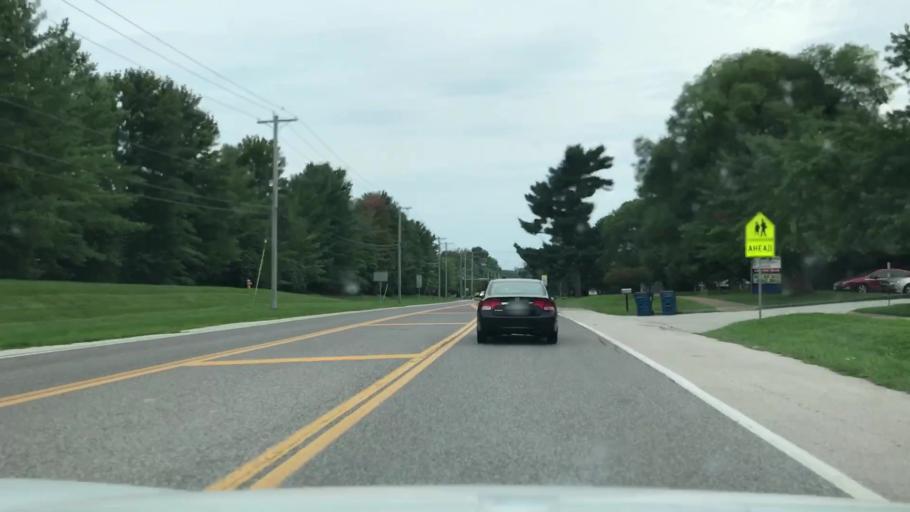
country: US
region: Missouri
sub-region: Saint Louis County
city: Chesterfield
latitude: 38.6594
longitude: -90.5824
